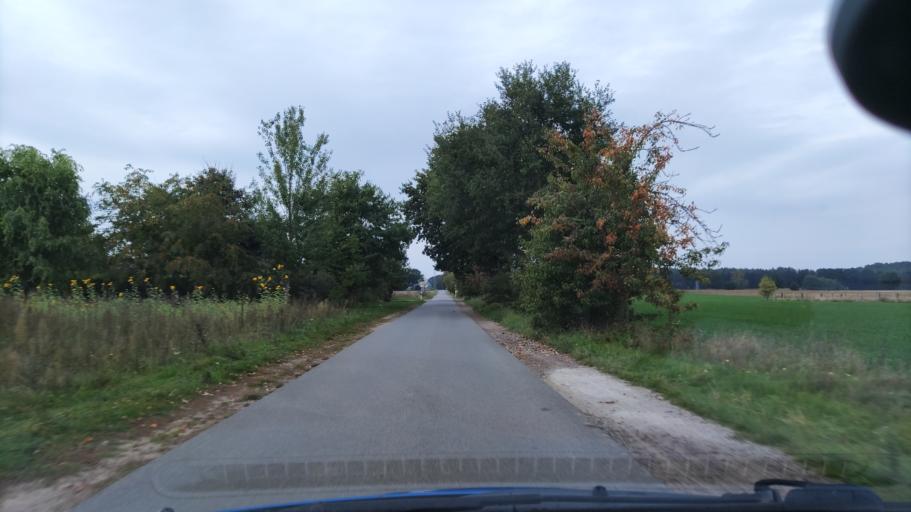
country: DE
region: Lower Saxony
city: Karwitz
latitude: 53.0917
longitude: 11.0137
